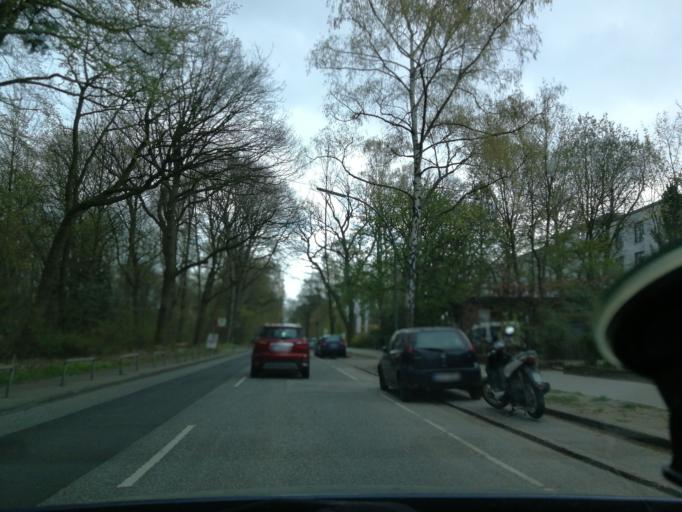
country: DE
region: Hamburg
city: Harburg
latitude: 53.4606
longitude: 9.9386
